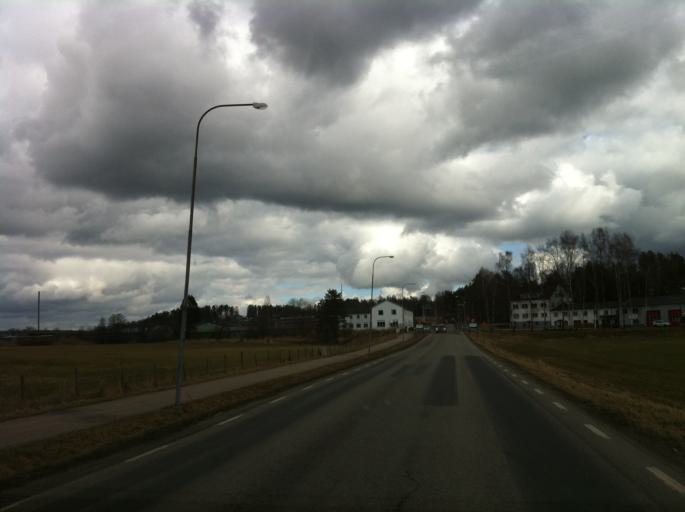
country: SE
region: Vaestra Goetaland
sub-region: Tranemo Kommun
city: Tranemo
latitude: 57.4696
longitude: 13.3307
